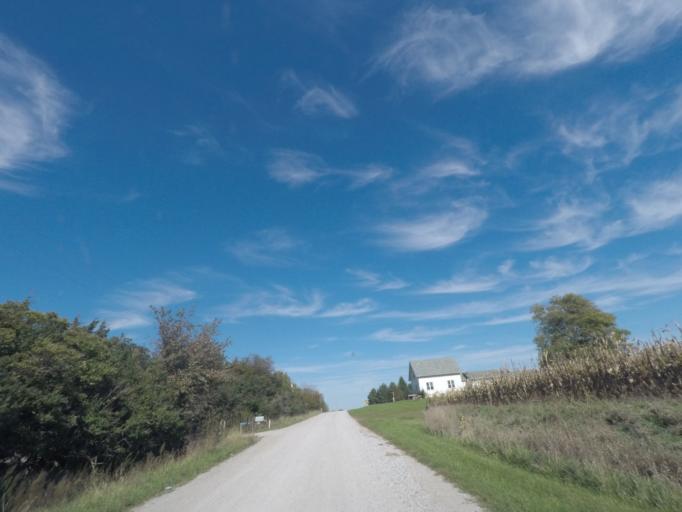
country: US
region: Iowa
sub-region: Story County
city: Nevada
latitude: 42.0097
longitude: -93.3476
